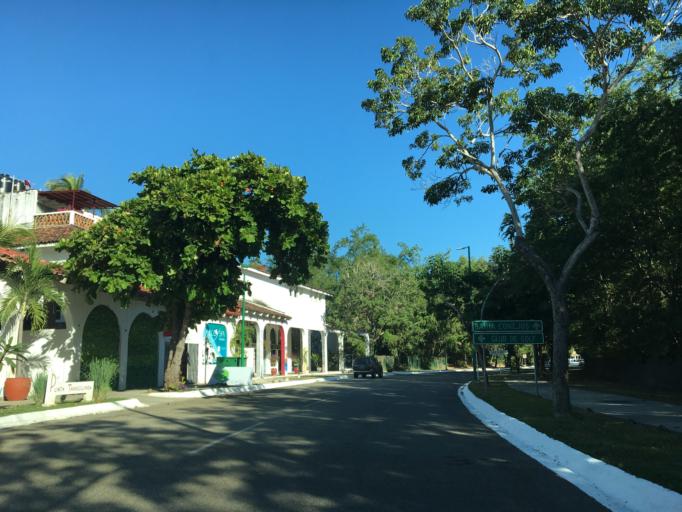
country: MX
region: Oaxaca
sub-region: Santa Maria Huatulco
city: Crucecita
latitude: 15.7753
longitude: -96.1003
